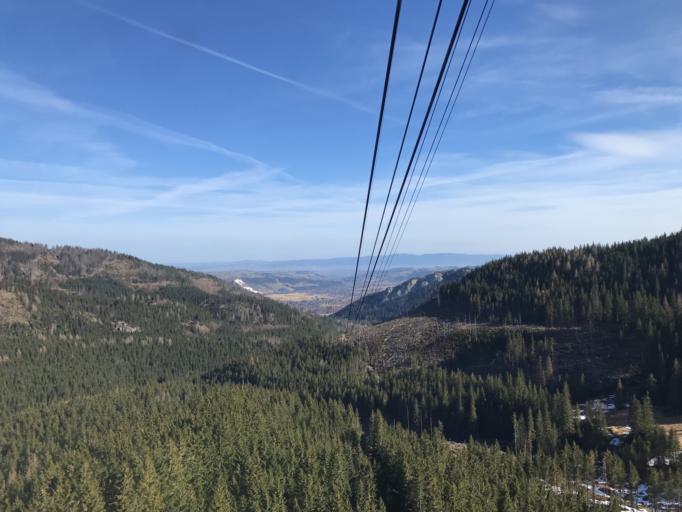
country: PL
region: Lesser Poland Voivodeship
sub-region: Powiat tatrzanski
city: Zakopane
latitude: 49.2539
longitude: 19.9744
